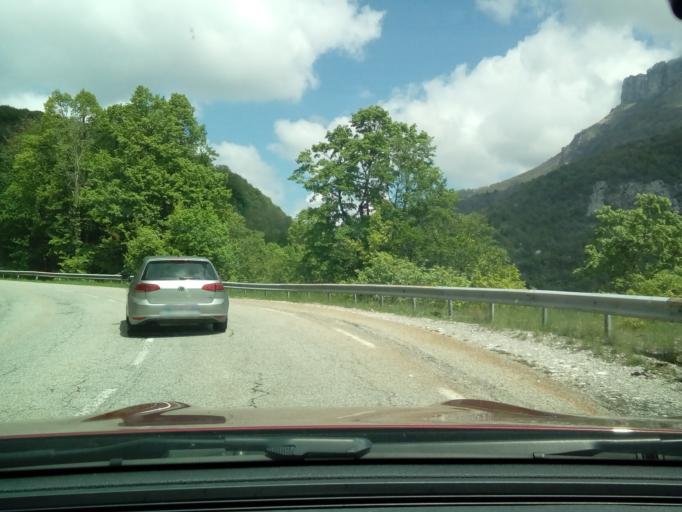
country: FR
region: Rhone-Alpes
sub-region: Departement de la Savoie
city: Barby
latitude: 45.6085
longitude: 6.0145
